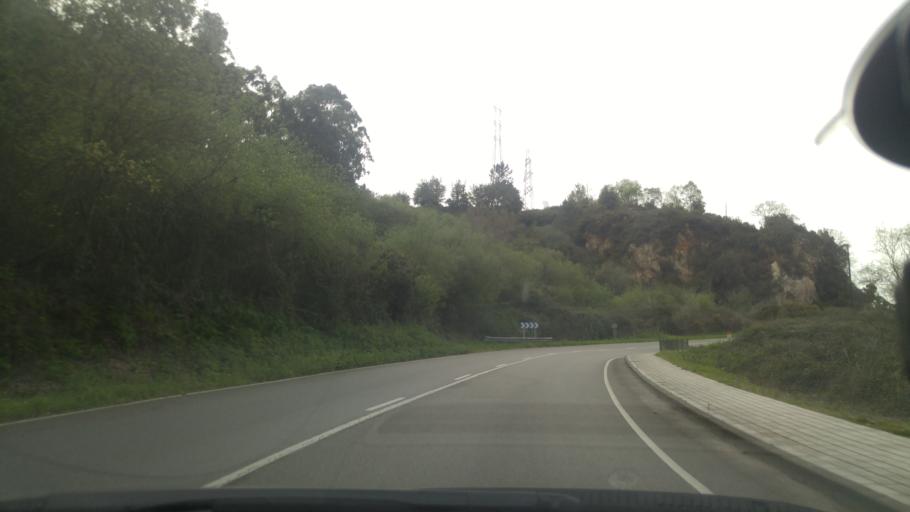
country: ES
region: Asturias
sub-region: Province of Asturias
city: Corvera de Asturias
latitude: 43.5284
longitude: -5.8790
